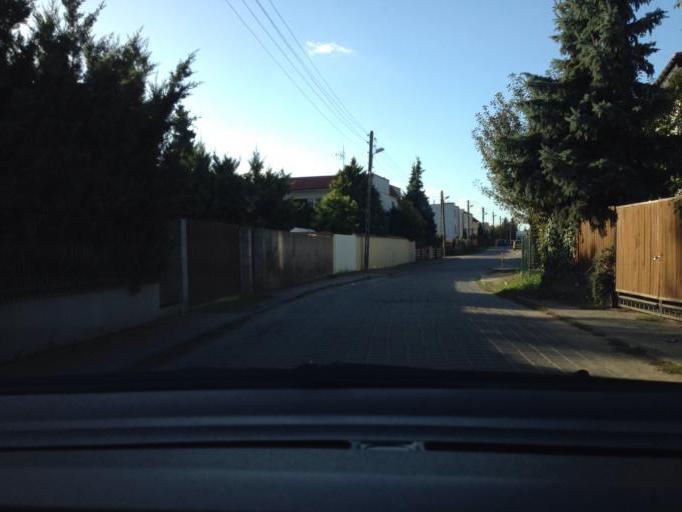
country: PL
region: Greater Poland Voivodeship
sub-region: Powiat poznanski
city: Suchy Las
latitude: 52.4586
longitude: 16.8792
